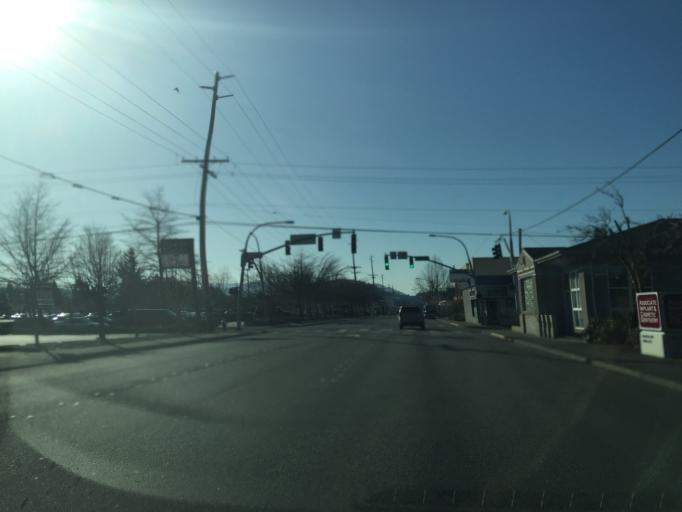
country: US
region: Washington
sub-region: Whatcom County
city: Bellingham
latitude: 48.7686
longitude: -122.4861
